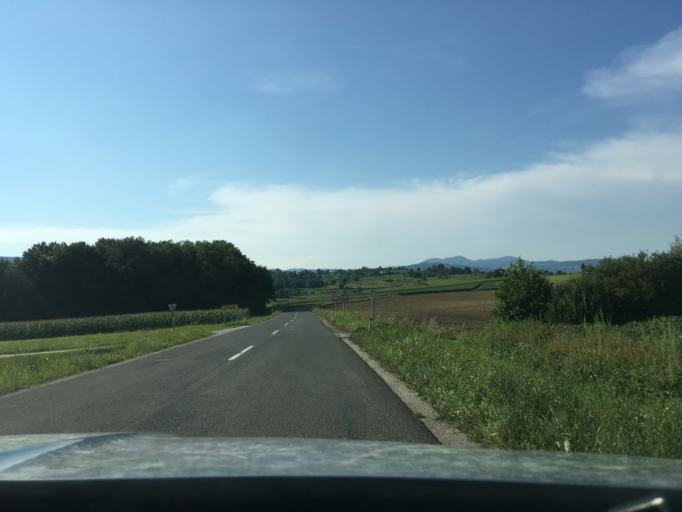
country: SI
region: Crnomelj
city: Crnomelj
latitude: 45.5238
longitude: 15.1658
